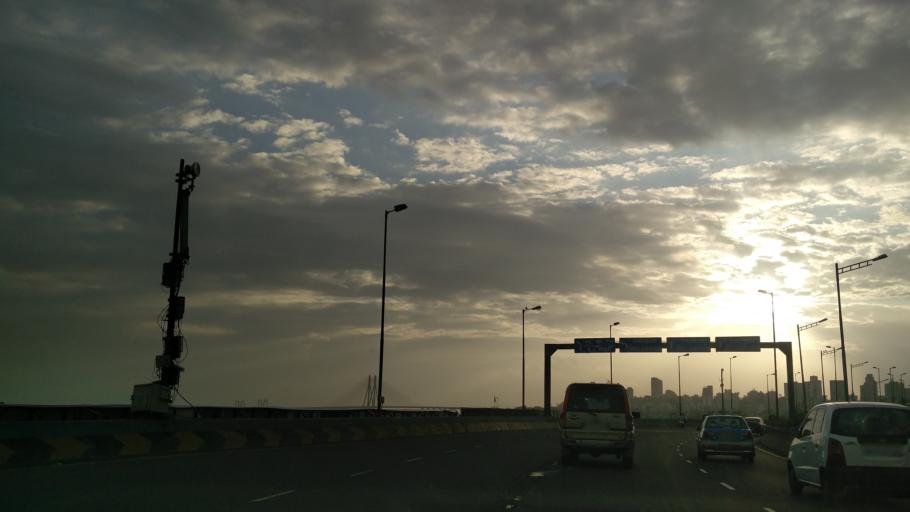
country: IN
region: Maharashtra
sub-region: Mumbai Suburban
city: Mumbai
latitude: 19.0499
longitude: 72.8386
